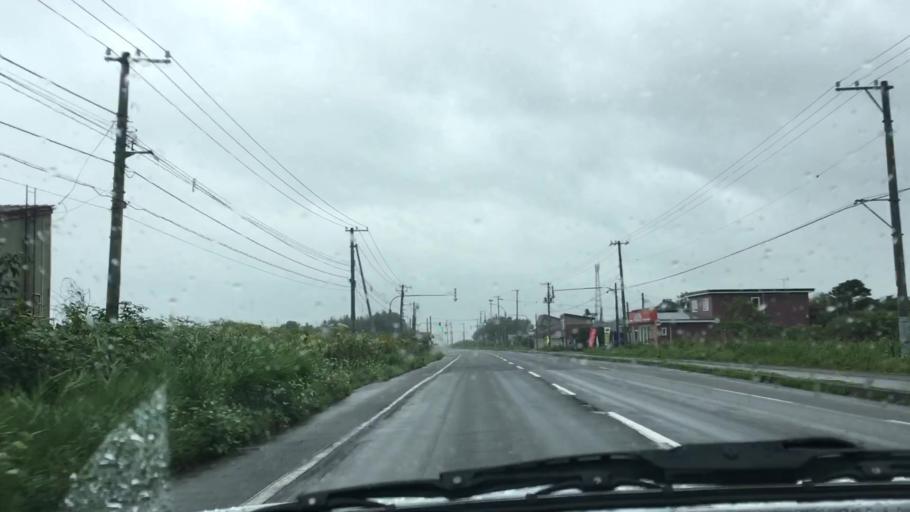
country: JP
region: Hokkaido
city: Nanae
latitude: 42.3161
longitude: 140.2742
